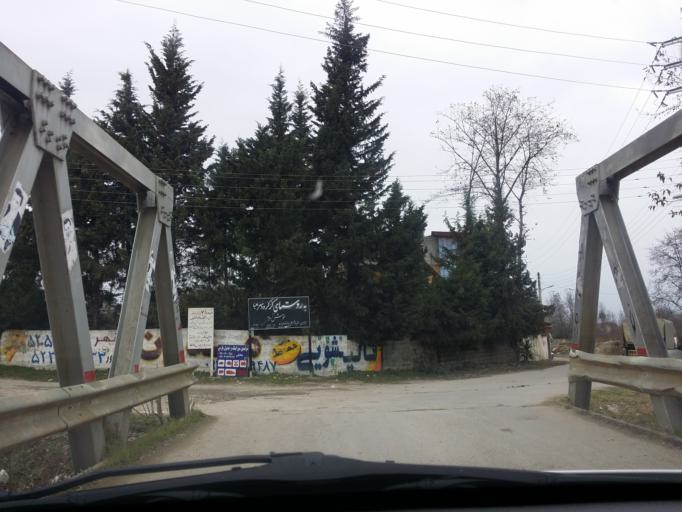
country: IR
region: Mazandaran
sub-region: Nowshahr
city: Nowshahr
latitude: 36.6455
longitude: 51.4797
